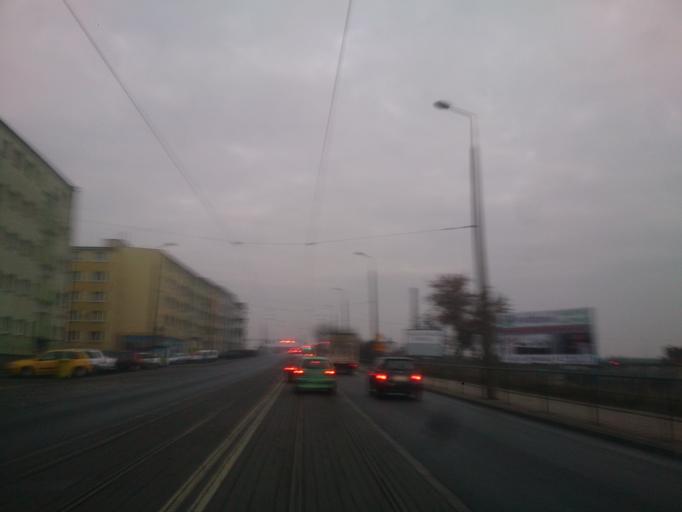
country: PL
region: Kujawsko-Pomorskie
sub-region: Grudziadz
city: Grudziadz
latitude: 53.4803
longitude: 18.7480
